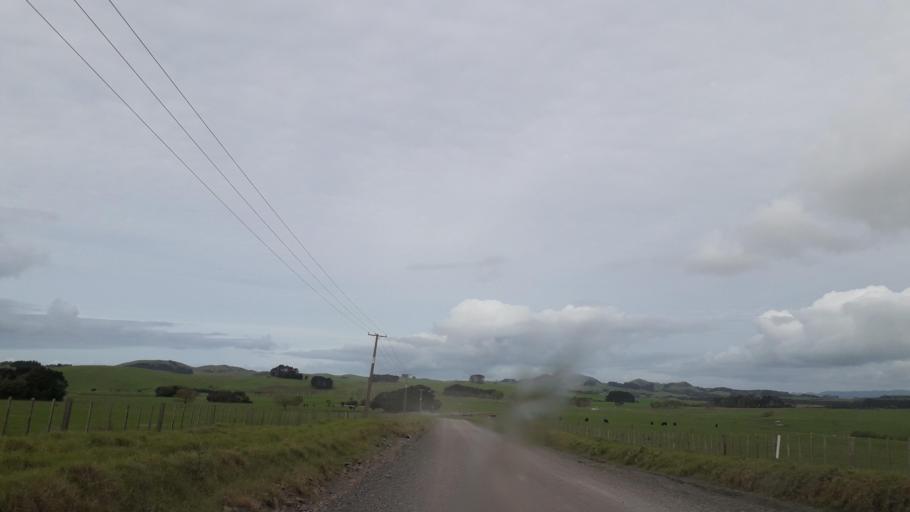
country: NZ
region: Northland
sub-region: Far North District
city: Kerikeri
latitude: -35.1364
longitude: 174.0257
